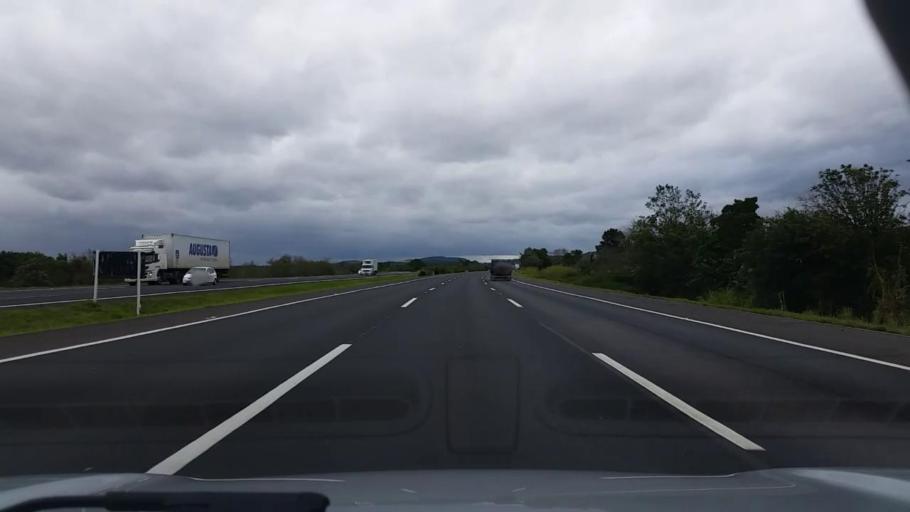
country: BR
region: Rio Grande do Sul
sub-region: Osorio
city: Osorio
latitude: -29.8799
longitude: -50.4326
